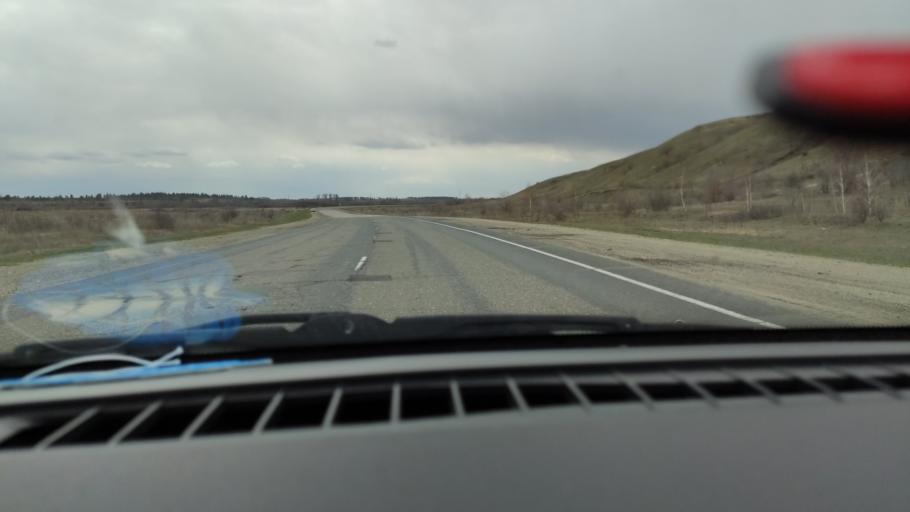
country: RU
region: Saratov
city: Sennoy
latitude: 52.0929
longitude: 46.8123
